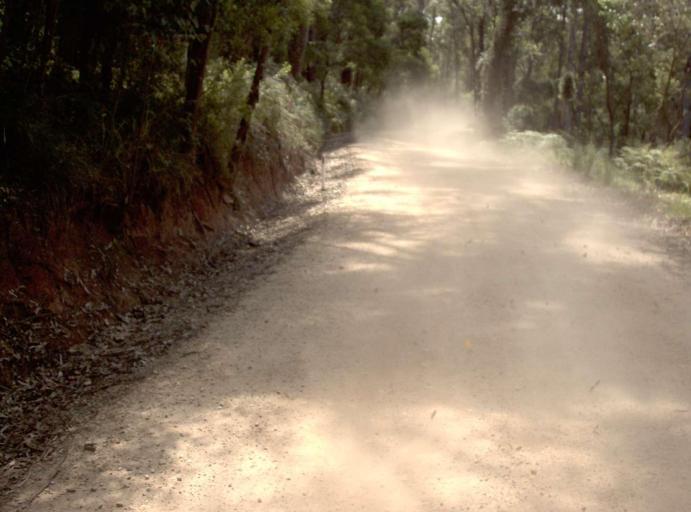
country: AU
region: Victoria
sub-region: East Gippsland
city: Lakes Entrance
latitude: -37.6216
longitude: 148.6913
